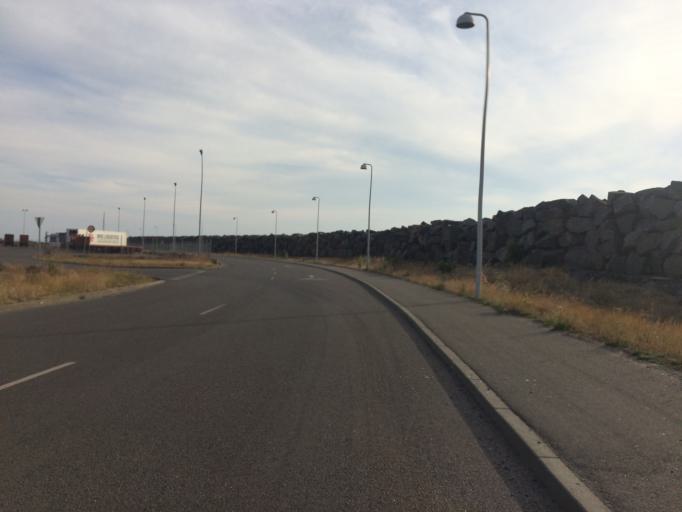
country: DK
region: Capital Region
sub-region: Bornholm Kommune
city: Ronne
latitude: 55.1030
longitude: 14.6870
